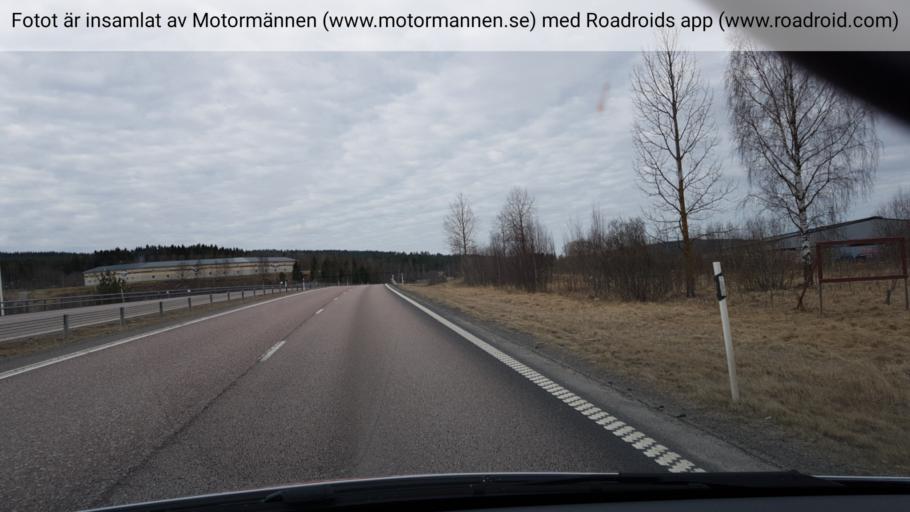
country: SE
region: Vaesternorrland
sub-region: OErnskoeldsviks Kommun
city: Ornskoldsvik
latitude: 63.3086
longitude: 18.7787
